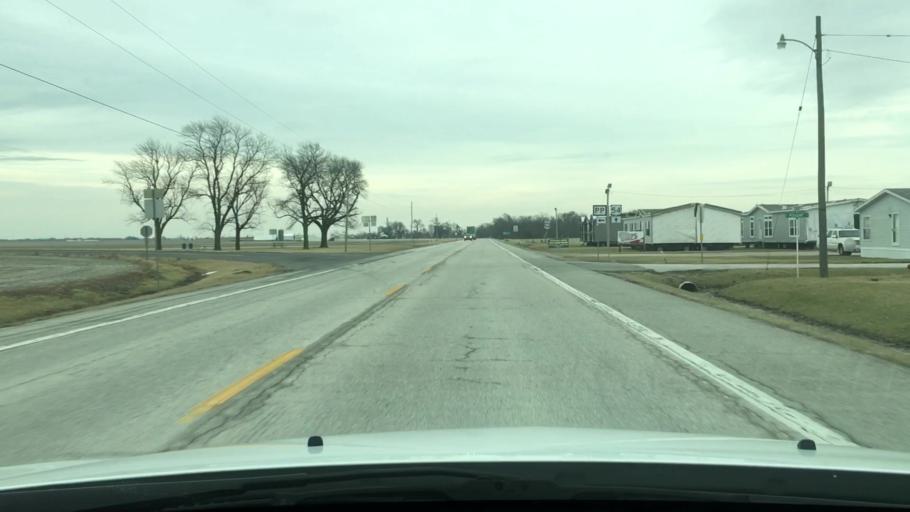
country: US
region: Missouri
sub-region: Audrain County
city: Vandalia
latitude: 39.2792
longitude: -91.5737
